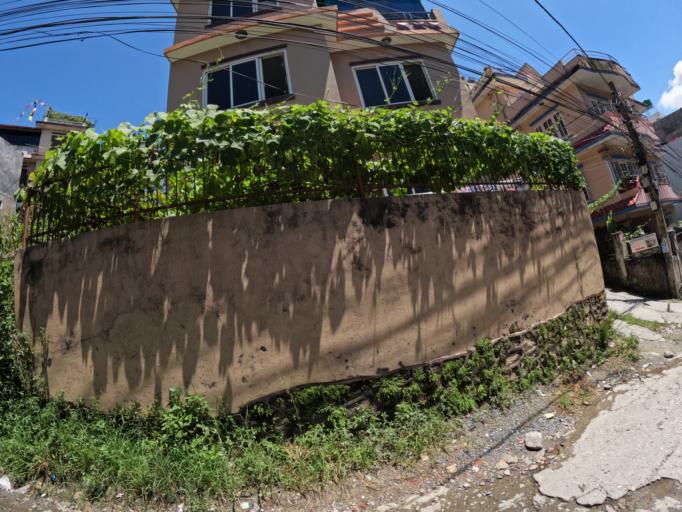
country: NP
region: Central Region
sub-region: Bagmati Zone
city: Kathmandu
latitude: 27.7417
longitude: 85.3257
